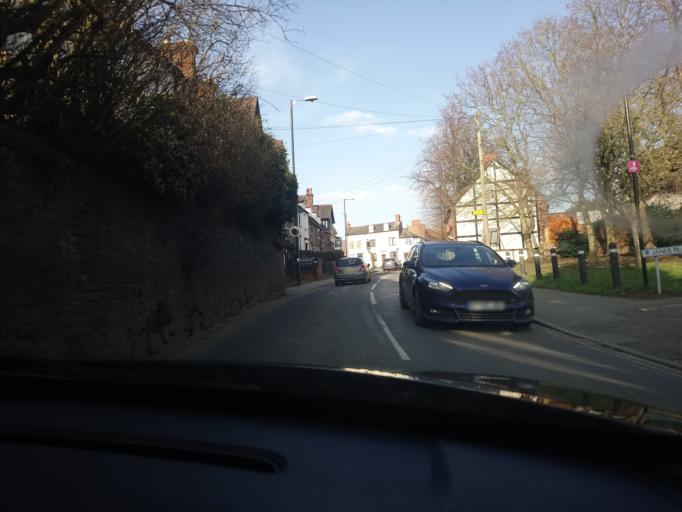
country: GB
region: England
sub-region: Shropshire
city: Shrewsbury
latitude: 52.7155
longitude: -2.7534
